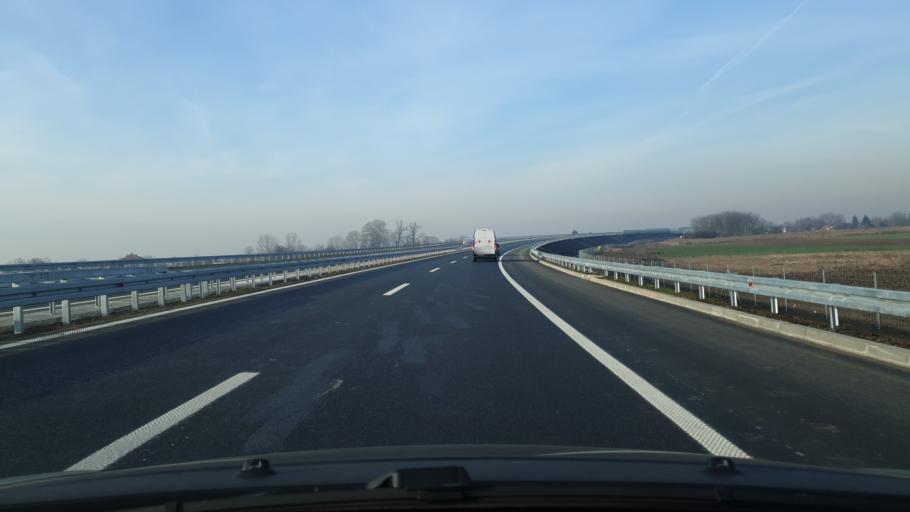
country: RS
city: Boljevci
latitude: 44.7281
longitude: 20.2490
